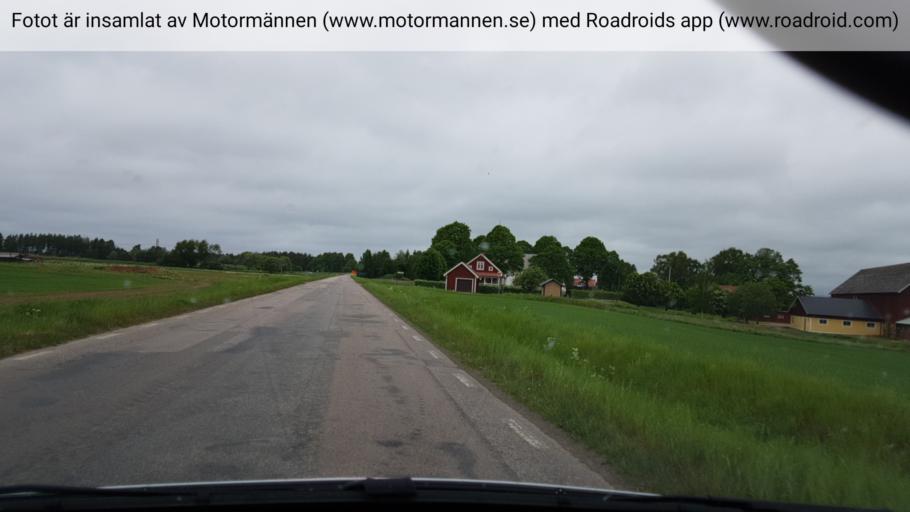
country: SE
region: Vaestra Goetaland
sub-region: Gotene Kommun
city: Kallby
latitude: 58.4924
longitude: 13.3153
